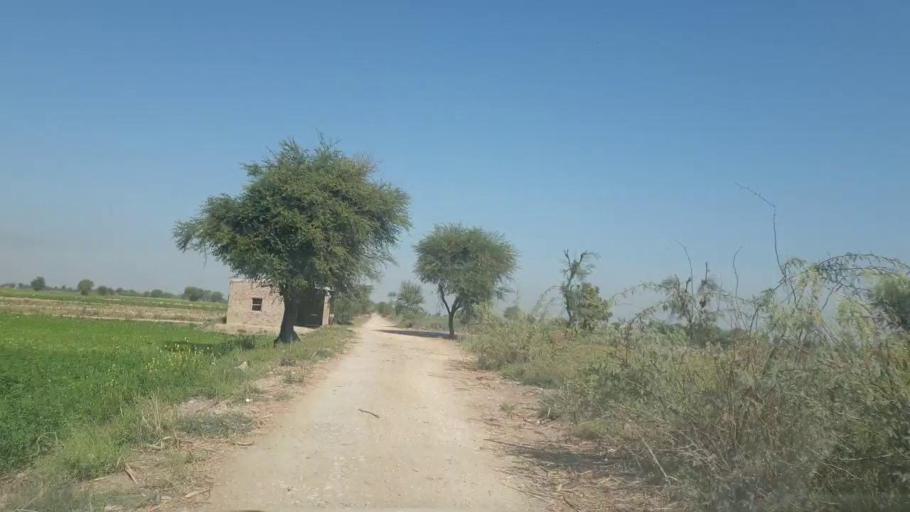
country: PK
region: Sindh
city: Mirpur Khas
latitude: 25.5463
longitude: 69.1965
